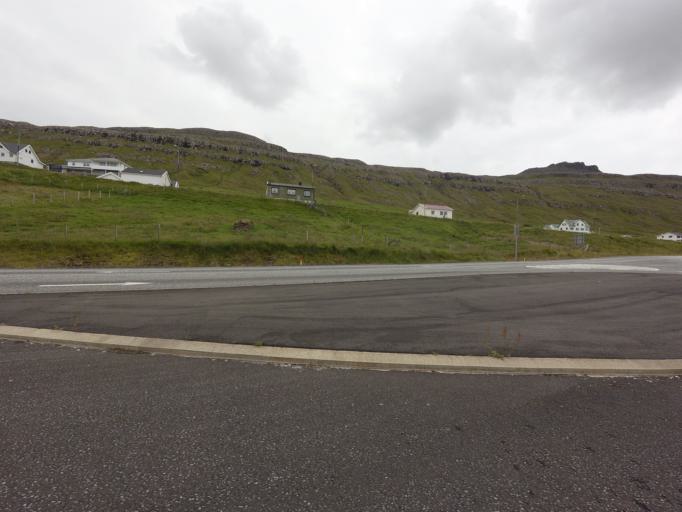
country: FO
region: Suduroy
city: Tvoroyri
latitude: 61.5482
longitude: -6.8194
